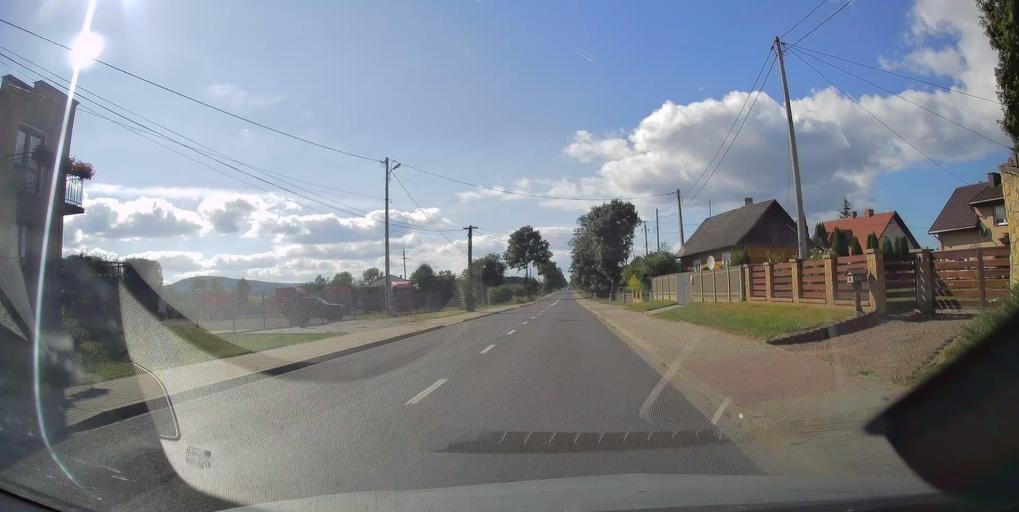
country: PL
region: Swietokrzyskie
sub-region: Powiat kielecki
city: Bodzentyn
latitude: 50.9454
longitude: 20.9393
